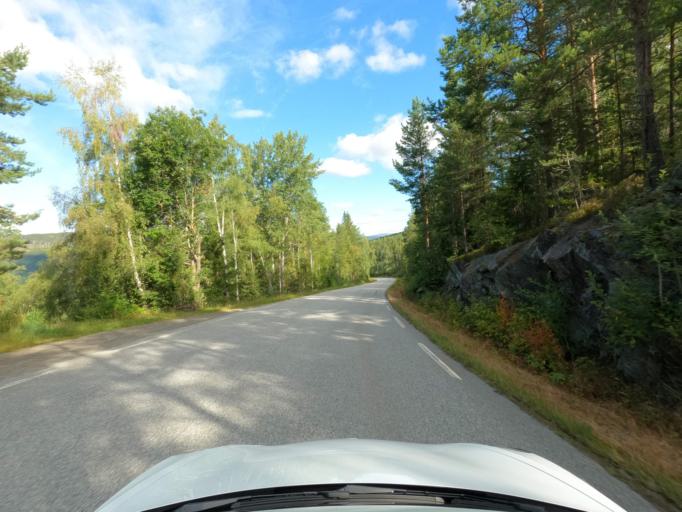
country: NO
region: Telemark
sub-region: Tinn
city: Rjukan
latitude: 59.9835
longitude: 8.8546
